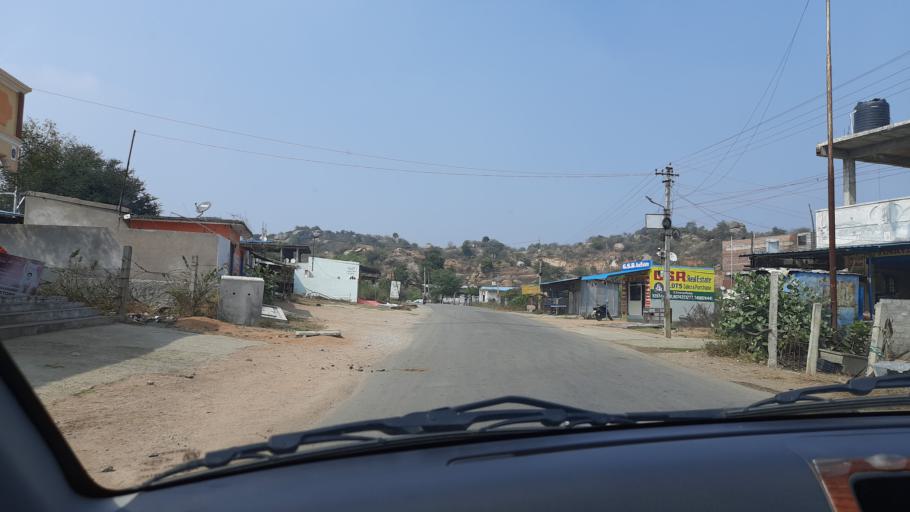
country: IN
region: Telangana
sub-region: Rangareddi
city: Lal Bahadur Nagar
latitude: 17.2742
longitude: 78.6677
